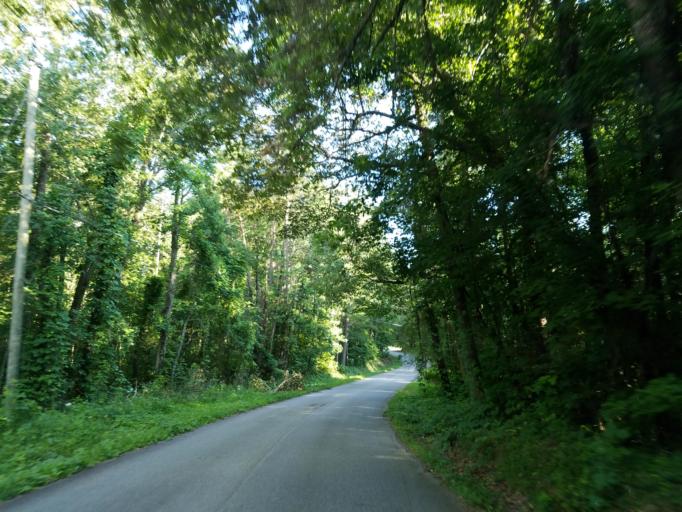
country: US
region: Georgia
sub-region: Gilmer County
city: Ellijay
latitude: 34.6377
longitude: -84.3312
